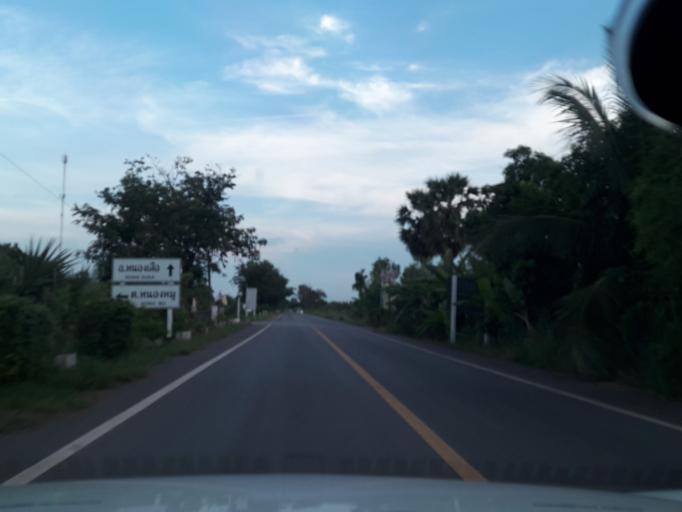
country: TH
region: Sara Buri
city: Nong Khae
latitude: 14.3063
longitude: 100.8875
